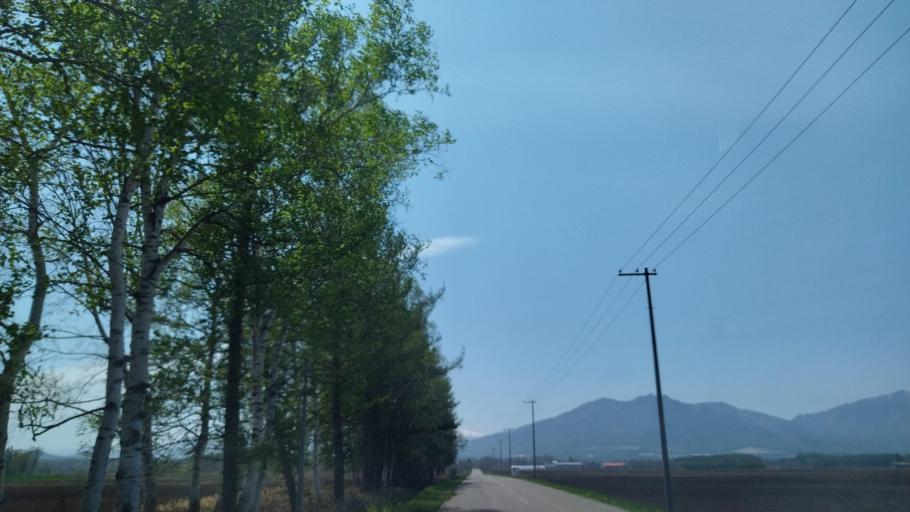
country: JP
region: Hokkaido
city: Obihiro
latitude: 42.9046
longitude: 142.9870
